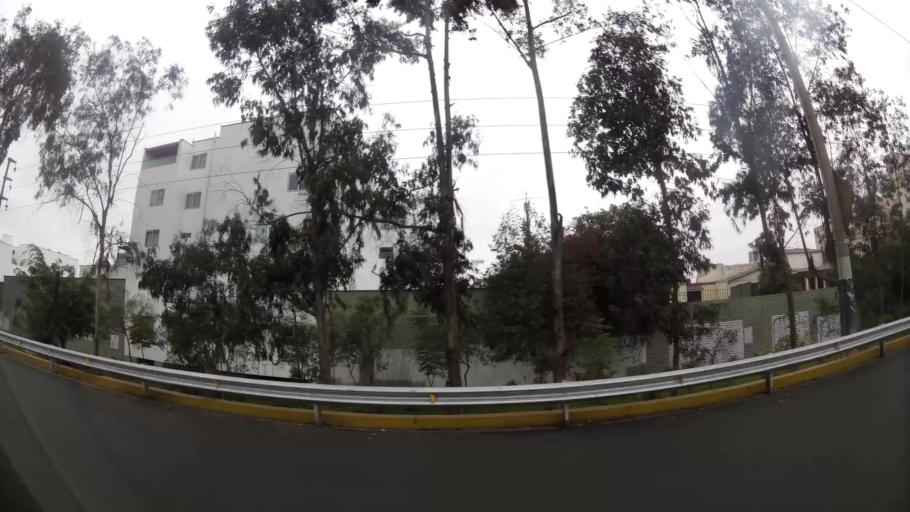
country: PE
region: Lima
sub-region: Lima
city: San Luis
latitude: -12.0896
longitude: -76.9813
